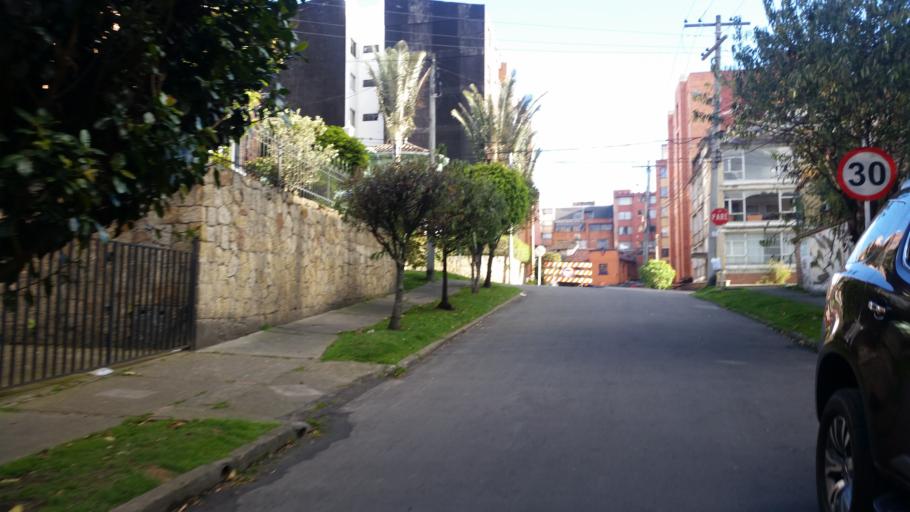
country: CO
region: Bogota D.C.
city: Bogota
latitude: 4.6408
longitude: -74.0615
